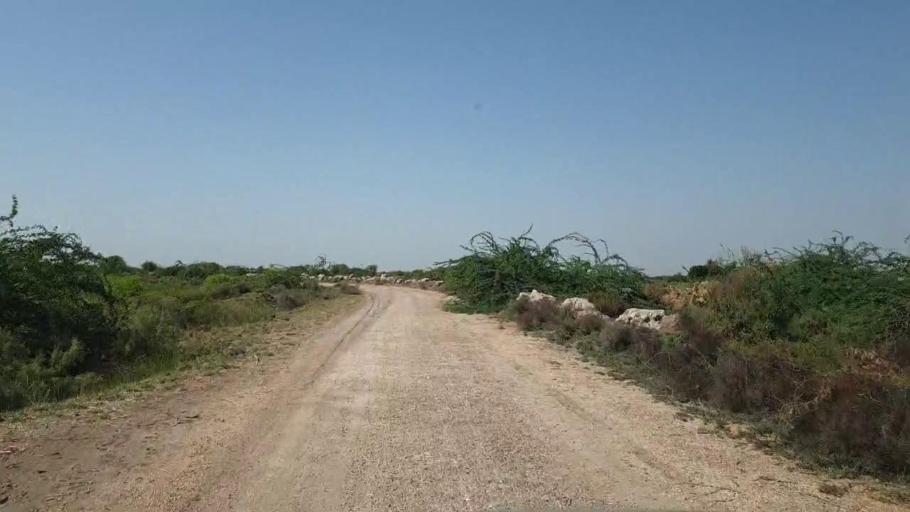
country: PK
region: Sindh
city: Tando Bago
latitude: 24.7059
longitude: 69.0557
